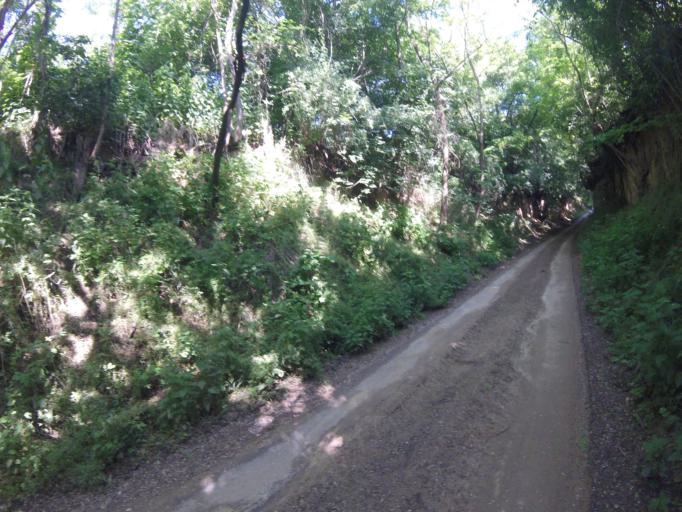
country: HU
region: Zala
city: Zalaszentgrot
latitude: 46.8875
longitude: 17.0701
